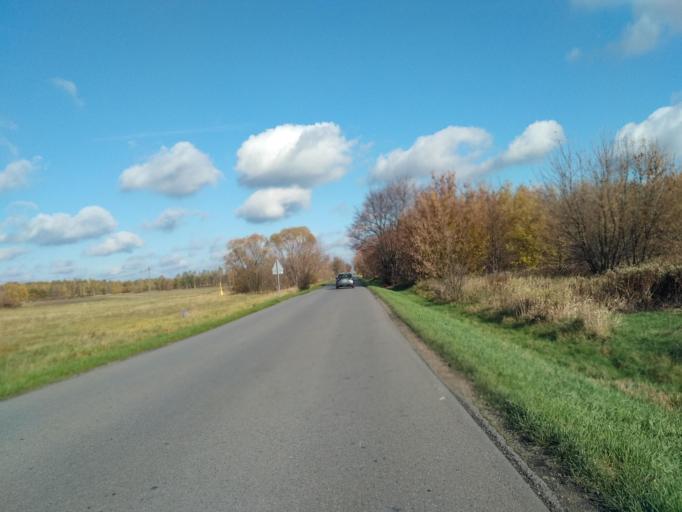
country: PL
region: Subcarpathian Voivodeship
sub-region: Powiat rzeszowski
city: Trzciana
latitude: 50.0914
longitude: 21.8470
